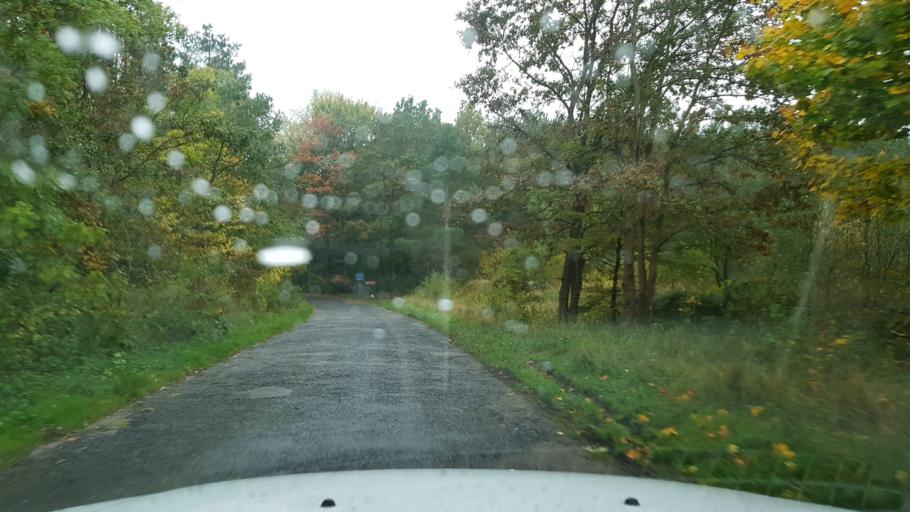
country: PL
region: West Pomeranian Voivodeship
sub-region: Powiat mysliborski
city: Barlinek
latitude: 53.0360
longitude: 15.2371
